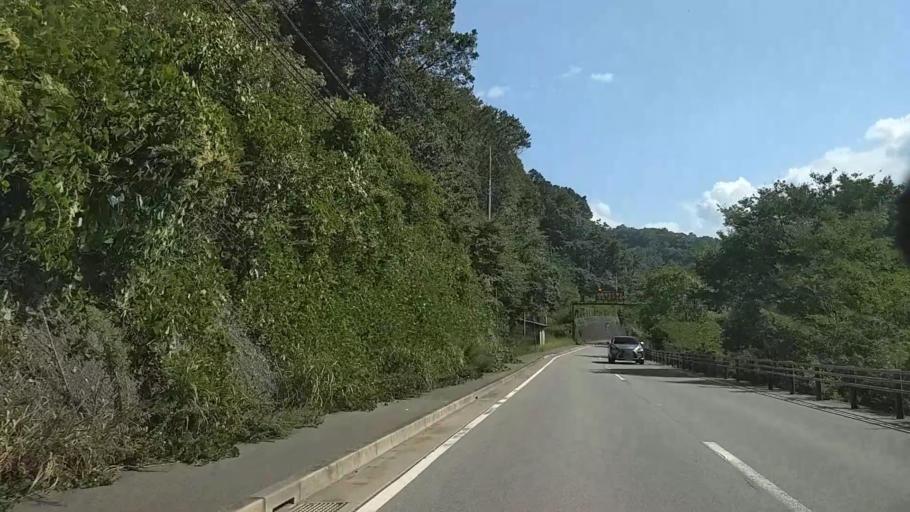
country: JP
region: Yamanashi
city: Ryuo
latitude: 35.4142
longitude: 138.4563
